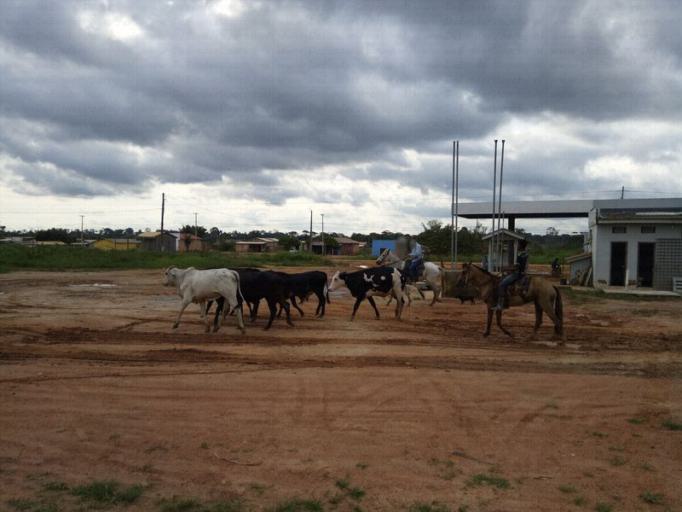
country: BR
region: Amazonas
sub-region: Humaita
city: Humaita
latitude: -6.9742
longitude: -63.0944
